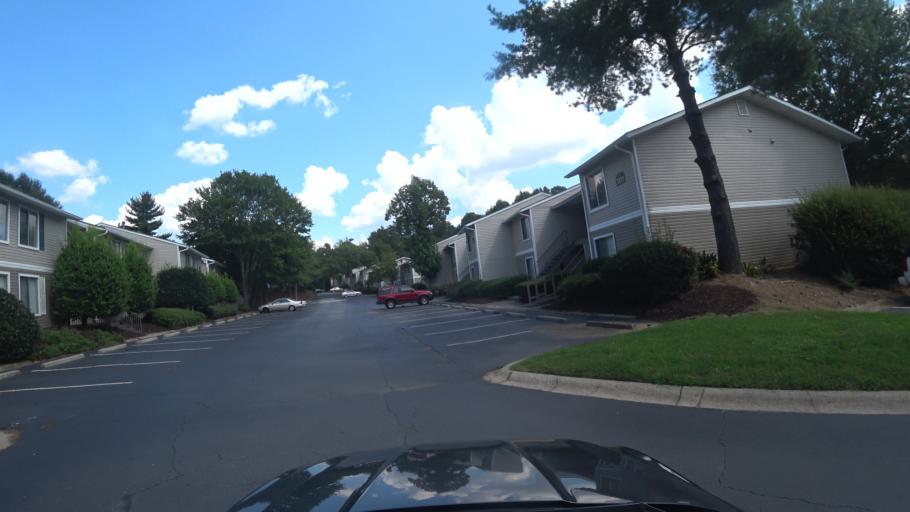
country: US
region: Georgia
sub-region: Gwinnett County
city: Norcross
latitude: 33.9539
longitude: -84.2559
